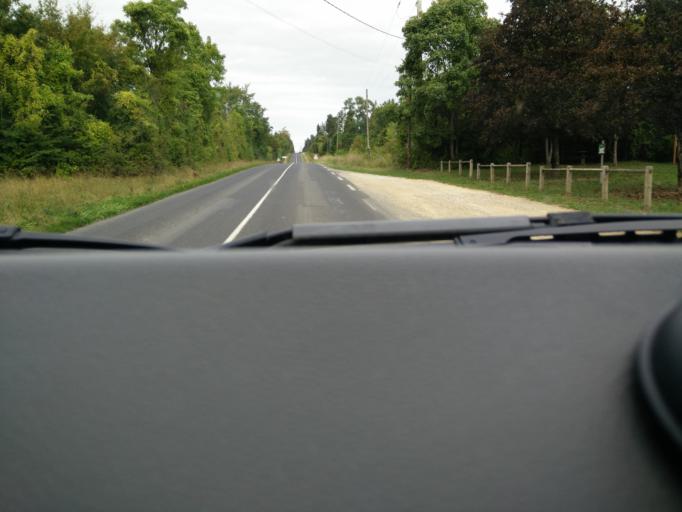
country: FR
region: Lorraine
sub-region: Departement de Meurthe-et-Moselle
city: Montauville
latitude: 48.9104
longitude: 5.9278
